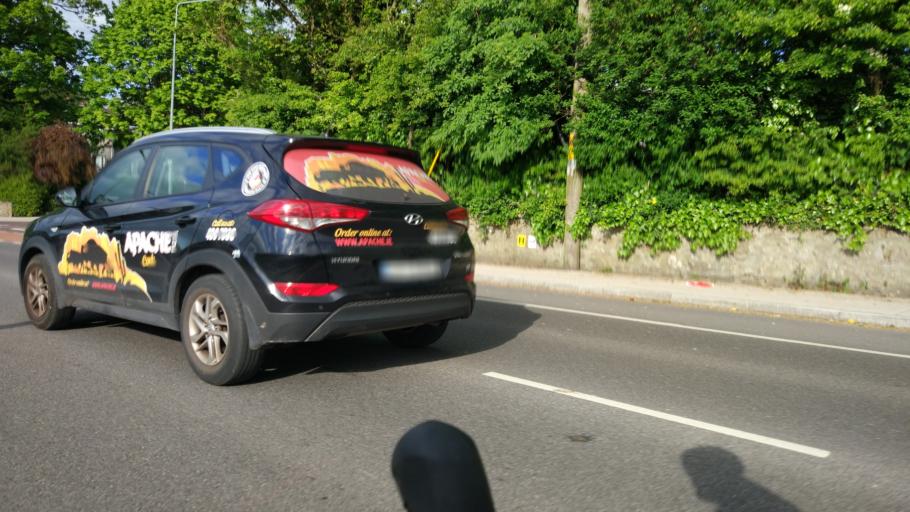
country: IE
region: Munster
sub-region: County Cork
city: Cork
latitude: 51.9134
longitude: -8.4477
